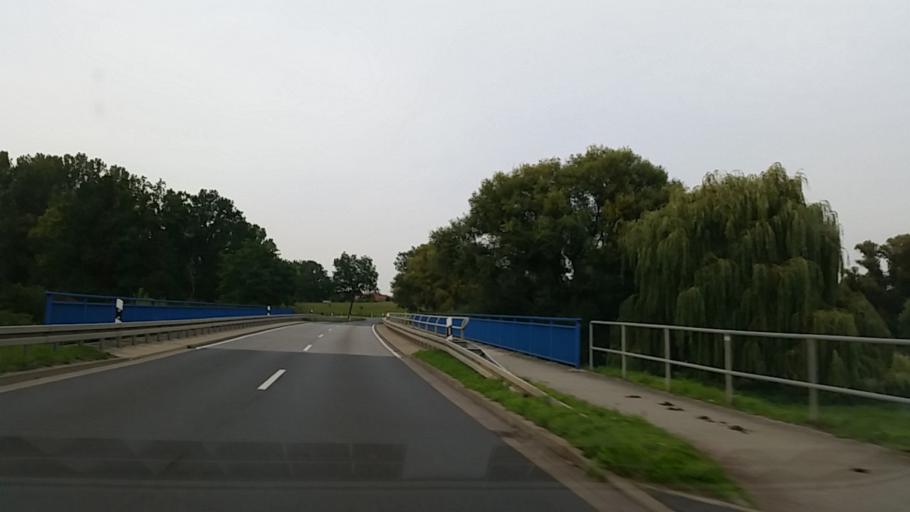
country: DE
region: Lower Saxony
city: Klein Schwulper
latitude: 52.3400
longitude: 10.4504
